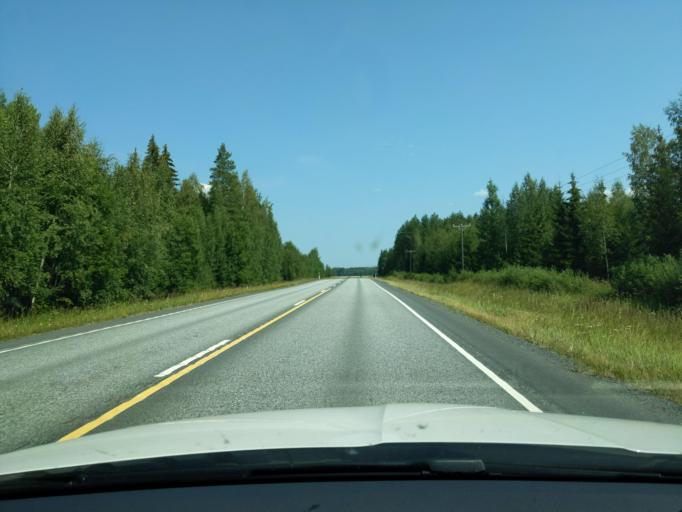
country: FI
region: Haeme
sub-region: Forssa
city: Ypaejae
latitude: 60.7407
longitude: 23.2724
